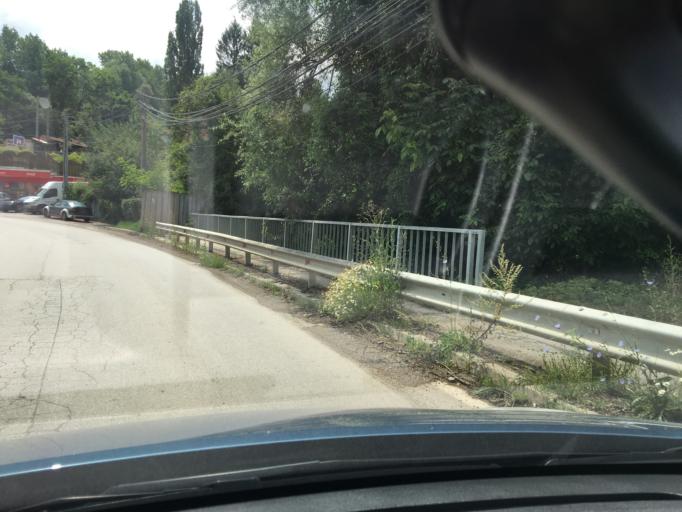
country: BG
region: Sofia-Capital
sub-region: Stolichna Obshtina
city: Sofia
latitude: 42.6107
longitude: 23.3633
